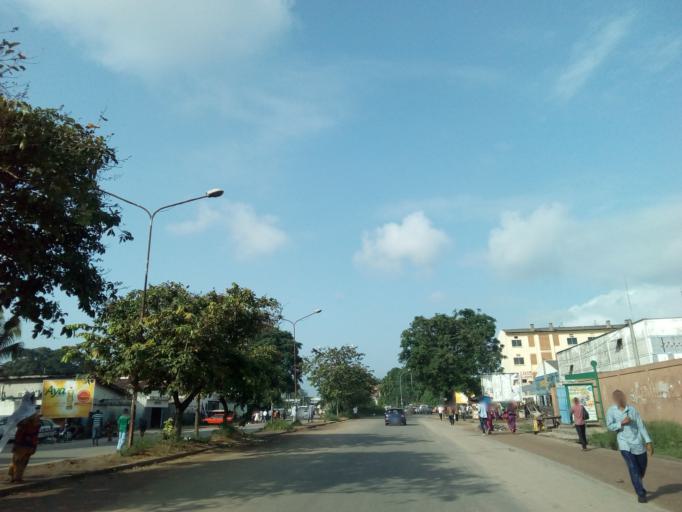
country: CI
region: Lagunes
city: Abidjan
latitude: 5.2964
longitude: -4.0032
